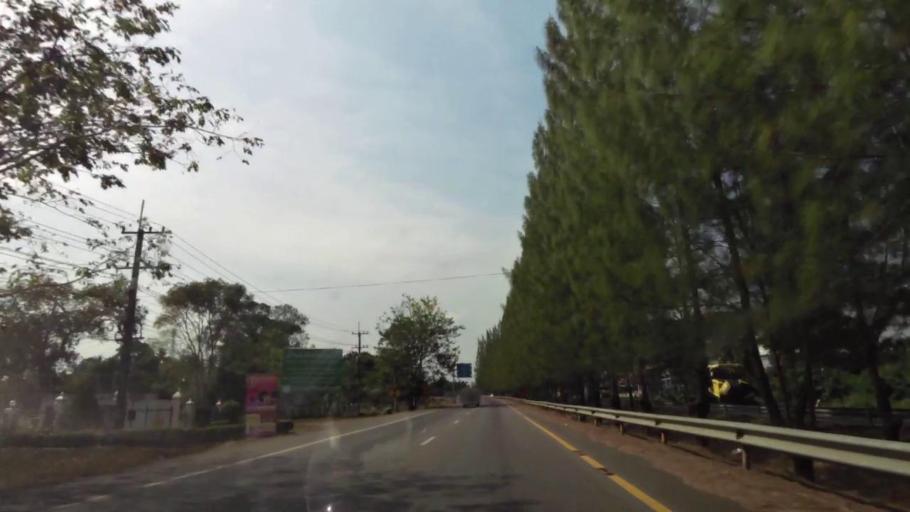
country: TH
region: Chanthaburi
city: Chanthaburi
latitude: 12.6666
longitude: 102.0971
